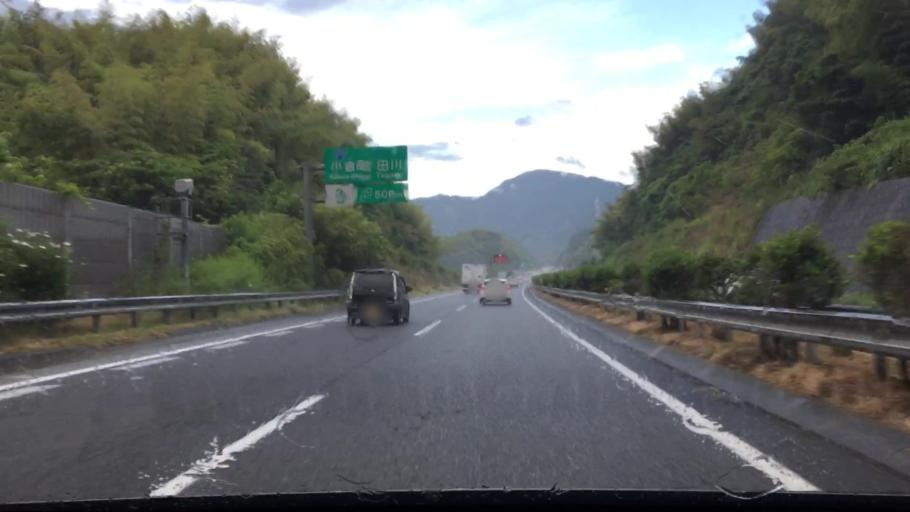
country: JP
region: Fukuoka
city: Kitakyushu
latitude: 33.8069
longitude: 130.8452
